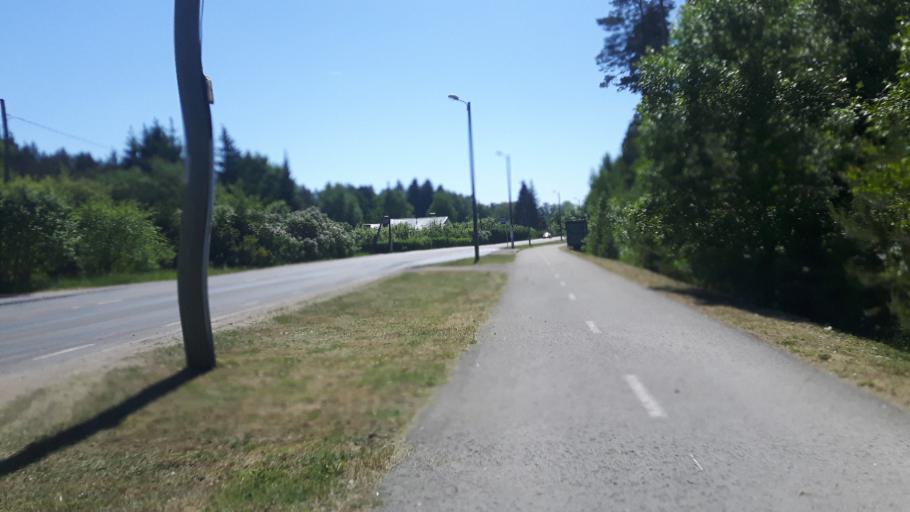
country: EE
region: Harju
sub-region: Saku vald
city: Saku
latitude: 59.2272
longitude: 24.6755
